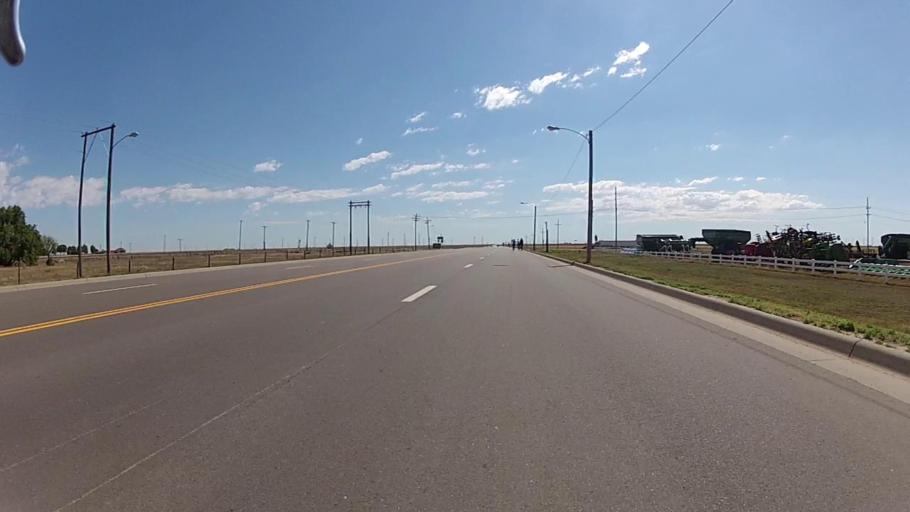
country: US
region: Kansas
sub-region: Gray County
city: Cimarron
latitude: 37.6013
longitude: -100.4350
